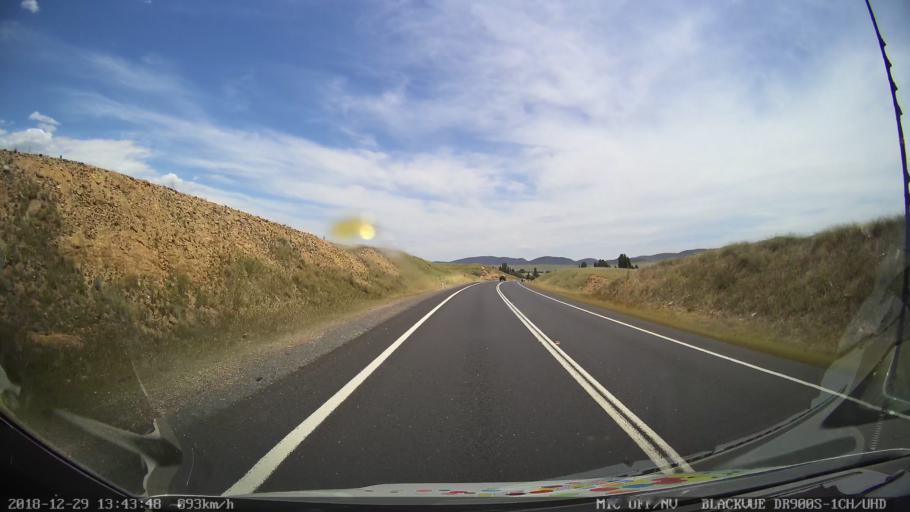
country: AU
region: New South Wales
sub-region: Cooma-Monaro
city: Cooma
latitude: -36.0774
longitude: 149.1597
